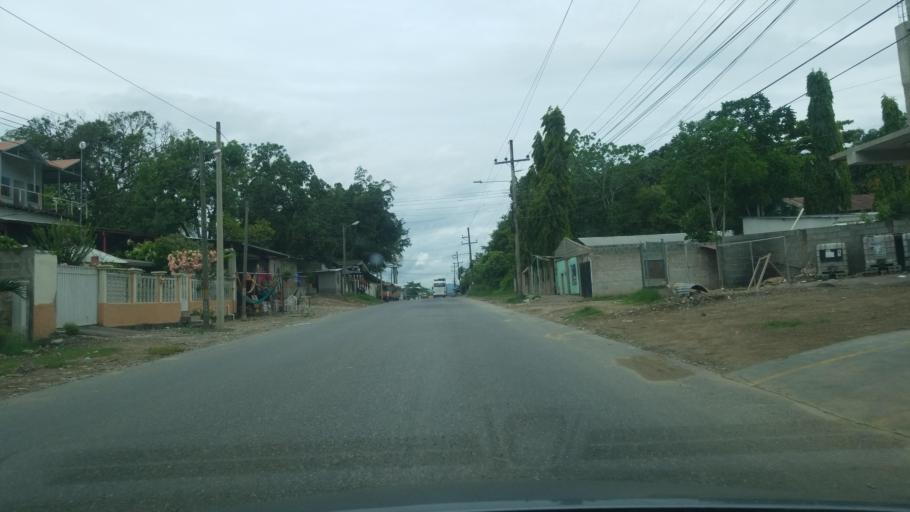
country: HN
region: Santa Barbara
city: La Flecha
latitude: 15.2959
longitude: -88.4869
